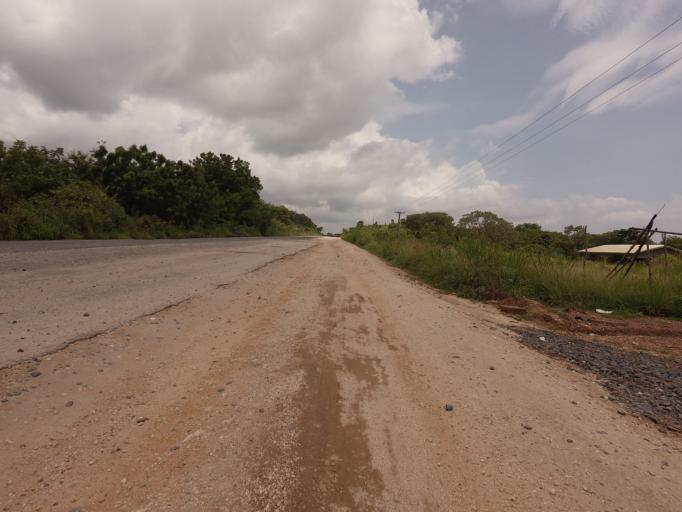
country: GH
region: Volta
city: Ho
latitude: 6.6752
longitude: 0.3130
